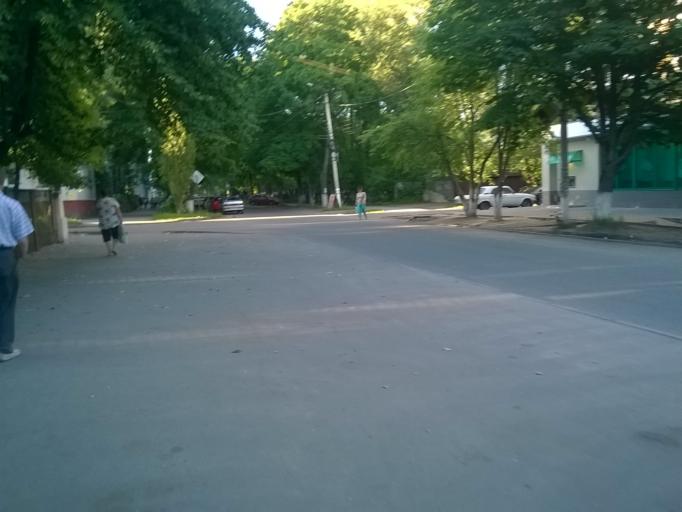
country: RU
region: Kursk
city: Kursk
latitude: 51.6700
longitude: 36.1502
